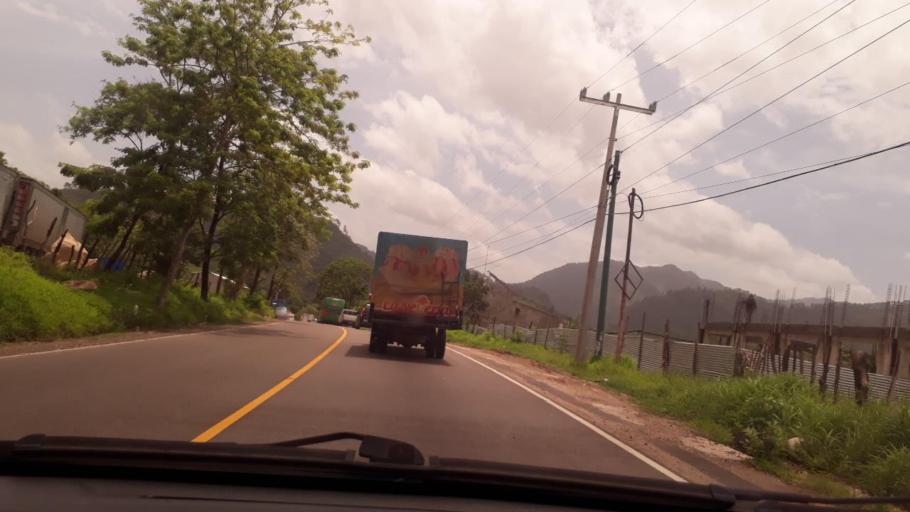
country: GT
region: Chiquimula
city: Quezaltepeque
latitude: 14.6291
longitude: -89.4507
